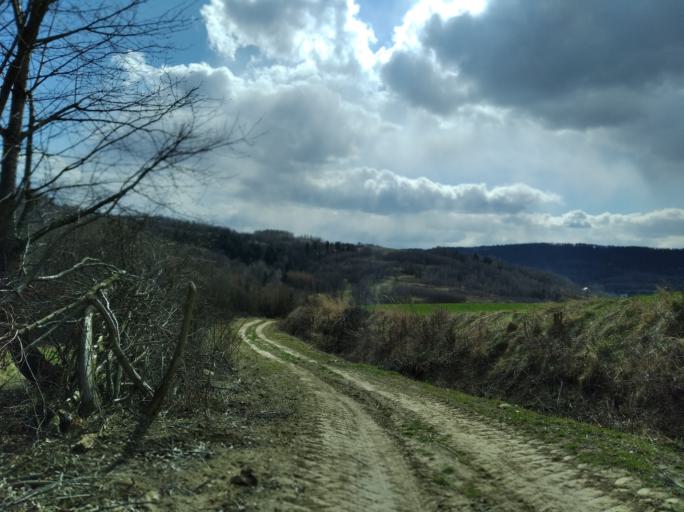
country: PL
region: Subcarpathian Voivodeship
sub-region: Powiat strzyzowski
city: Jawornik
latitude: 49.8352
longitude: 21.8442
